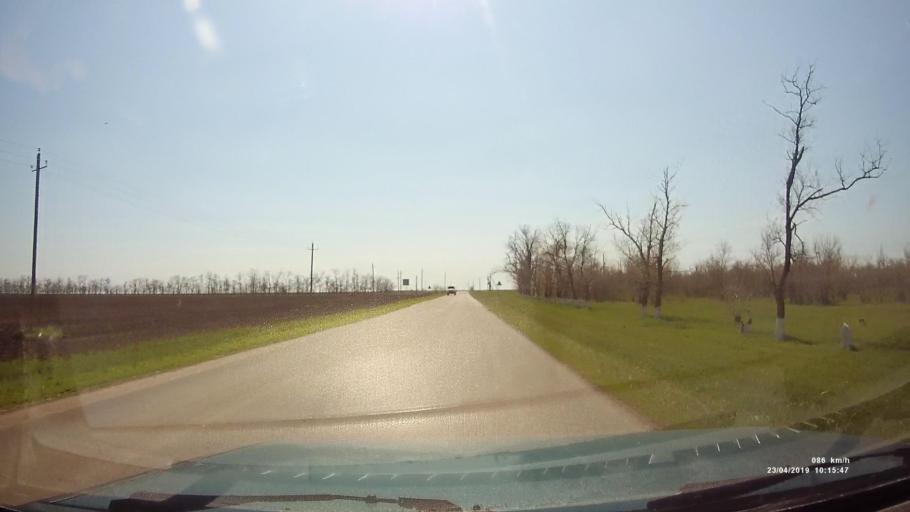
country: RU
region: Rostov
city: Sovetskoye
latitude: 46.6639
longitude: 42.3854
